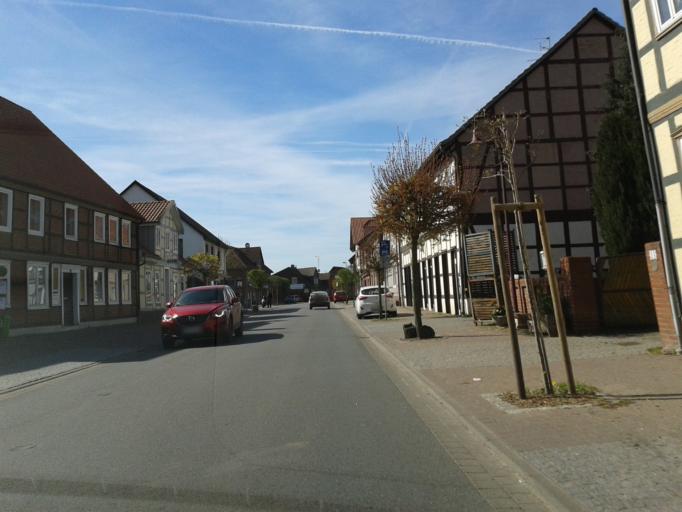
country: DE
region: Lower Saxony
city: Clenze
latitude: 52.9337
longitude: 10.9539
